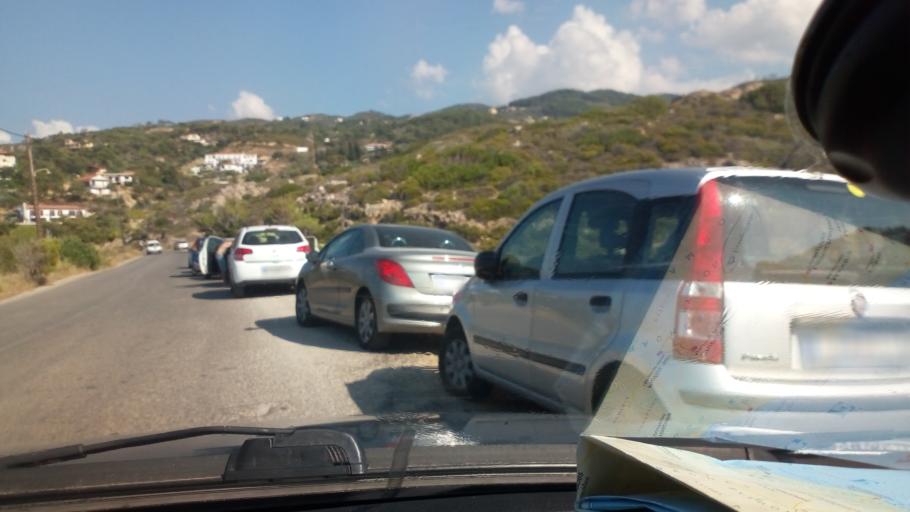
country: GR
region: North Aegean
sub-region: Nomos Samou
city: Agios Kirykos
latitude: 37.6297
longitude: 26.0998
